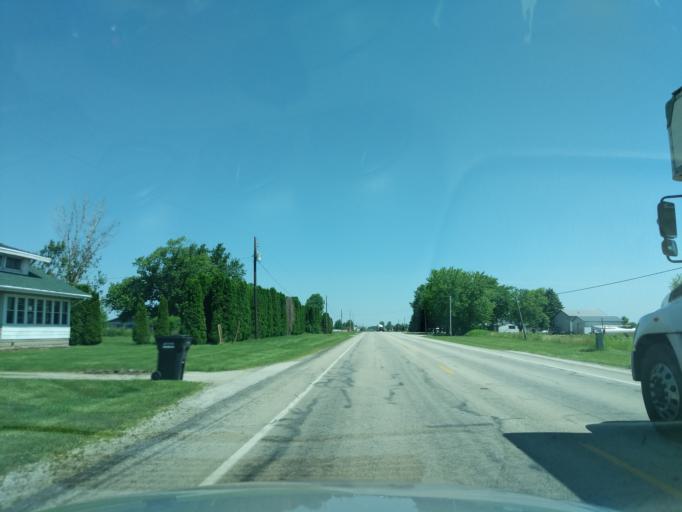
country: US
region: Indiana
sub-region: Whitley County
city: Columbia City
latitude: 41.0681
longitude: -85.4704
